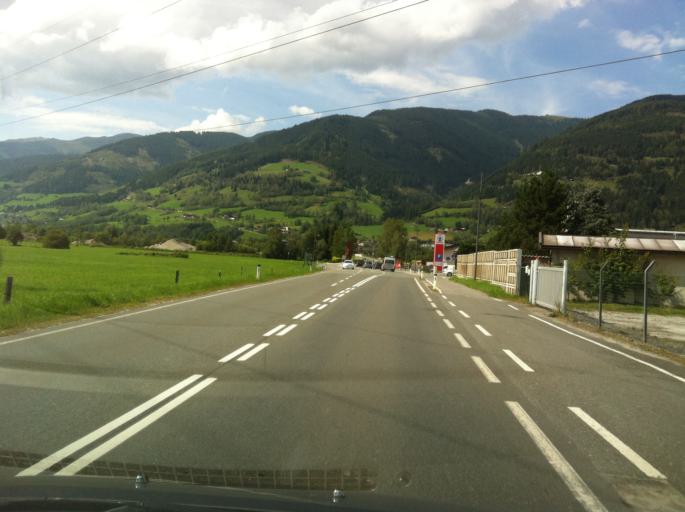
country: AT
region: Salzburg
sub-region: Politischer Bezirk Zell am See
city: Kaprun
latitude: 47.2813
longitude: 12.7547
